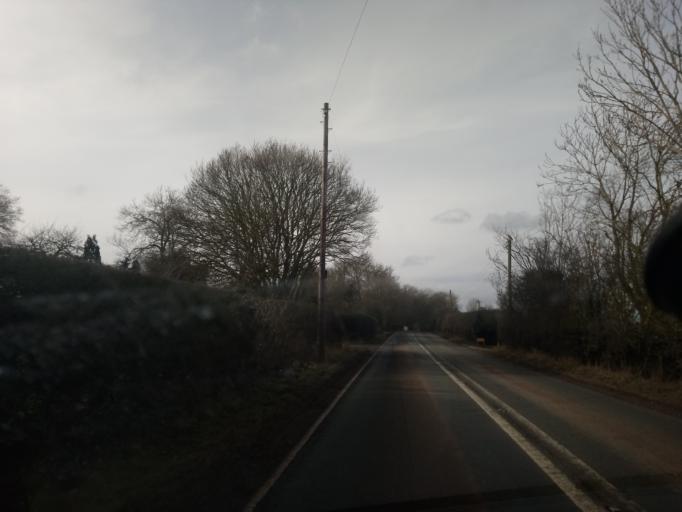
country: GB
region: England
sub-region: Shropshire
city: Prees
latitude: 52.8762
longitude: -2.6167
